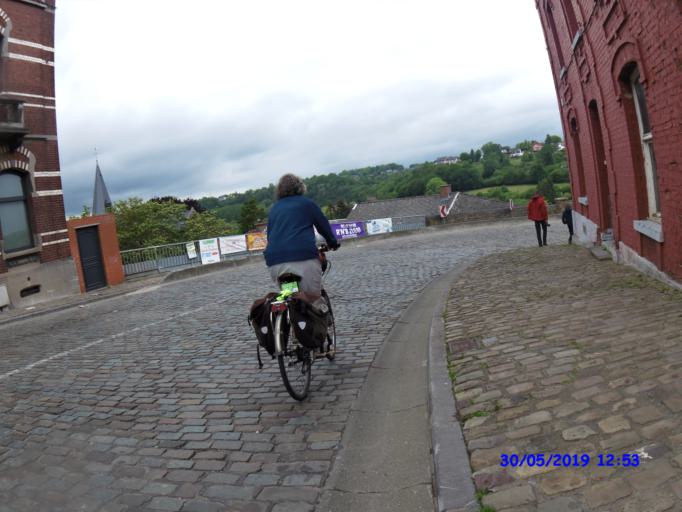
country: BE
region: Wallonia
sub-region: Province du Hainaut
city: Thuin
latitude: 50.3405
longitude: 4.2827
